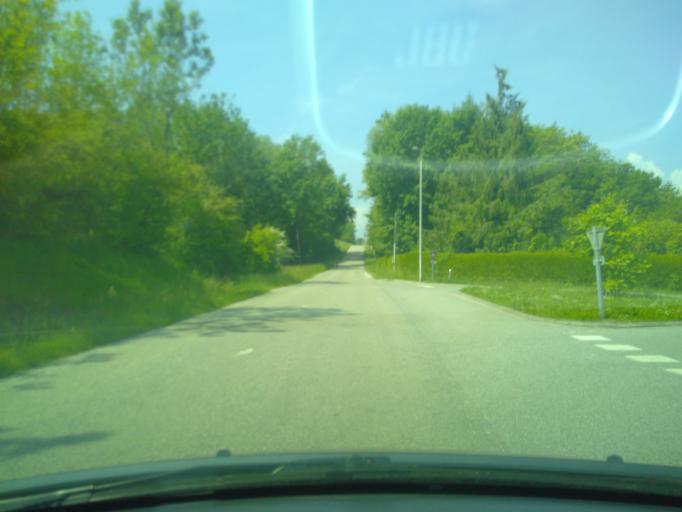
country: FR
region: Rhone-Alpes
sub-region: Departement de la Haute-Savoie
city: Archamps
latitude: 46.1240
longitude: 6.1392
